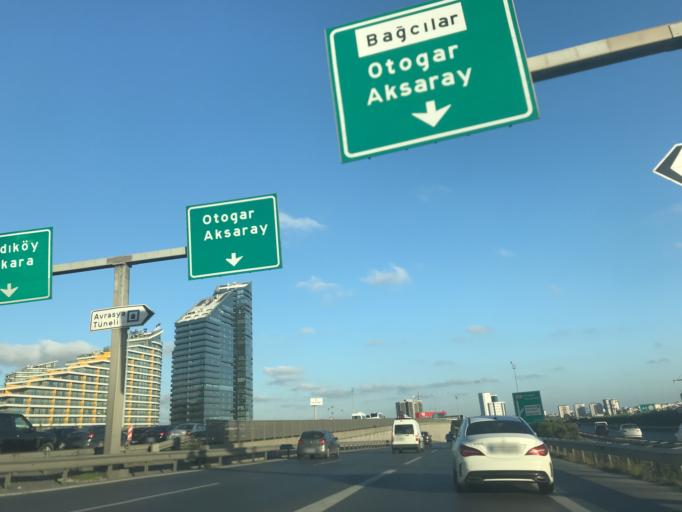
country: TR
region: Istanbul
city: Mahmutbey
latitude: 41.0630
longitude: 28.8381
